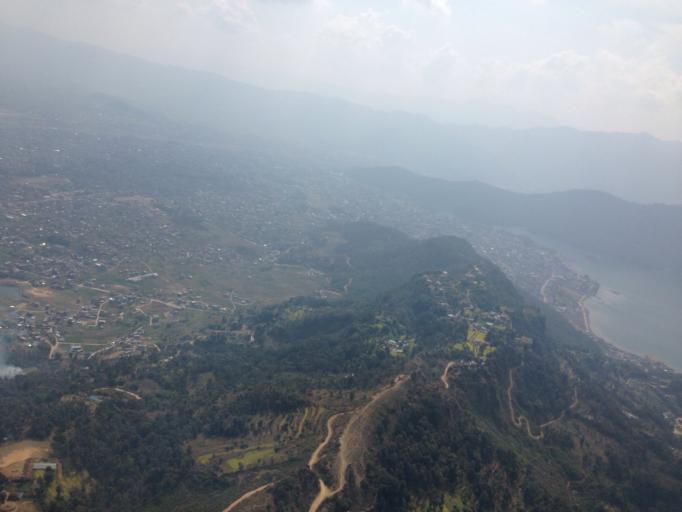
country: NP
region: Western Region
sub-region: Gandaki Zone
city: Pokhara
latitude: 28.2388
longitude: 83.9667
